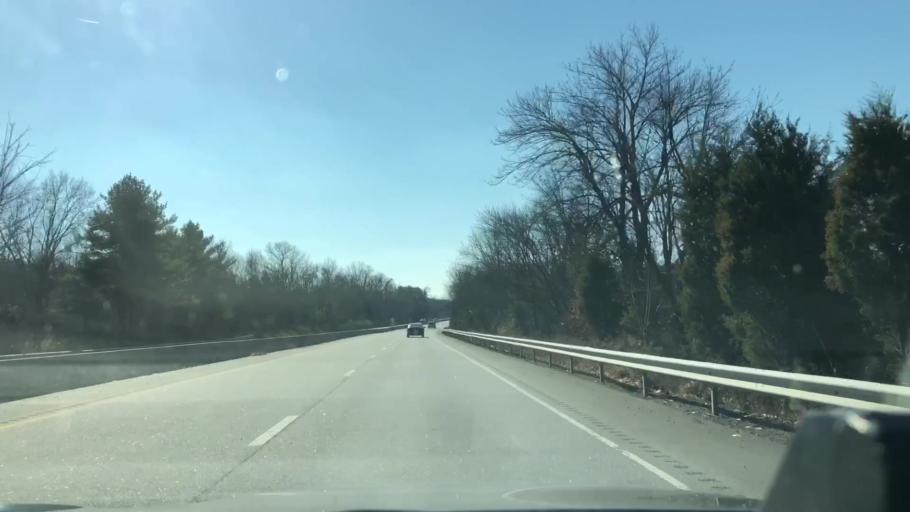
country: US
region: Pennsylvania
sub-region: Montgomery County
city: Halfway House
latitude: 40.2858
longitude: -75.6442
